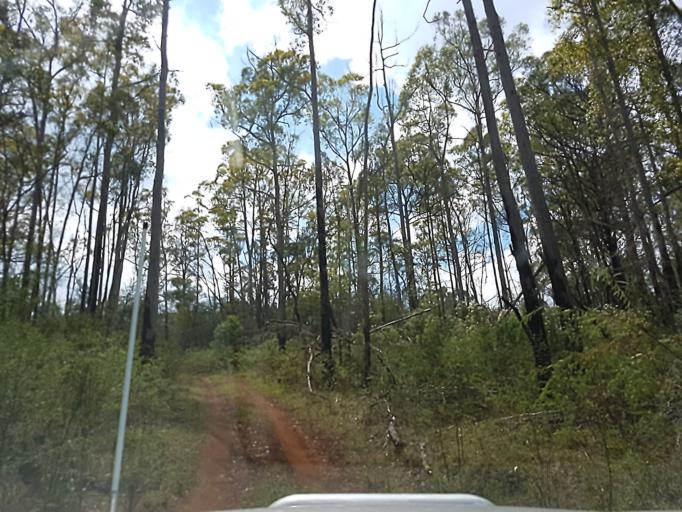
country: AU
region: Victoria
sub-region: East Gippsland
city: Lakes Entrance
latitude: -37.3587
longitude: 148.3565
